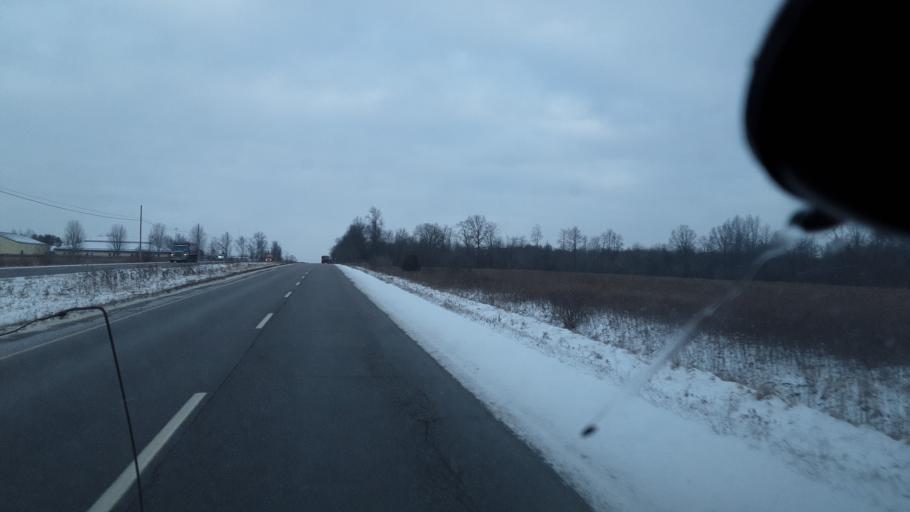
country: US
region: Ohio
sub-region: Trumbull County
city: Lordstown
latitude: 41.1247
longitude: -80.8874
